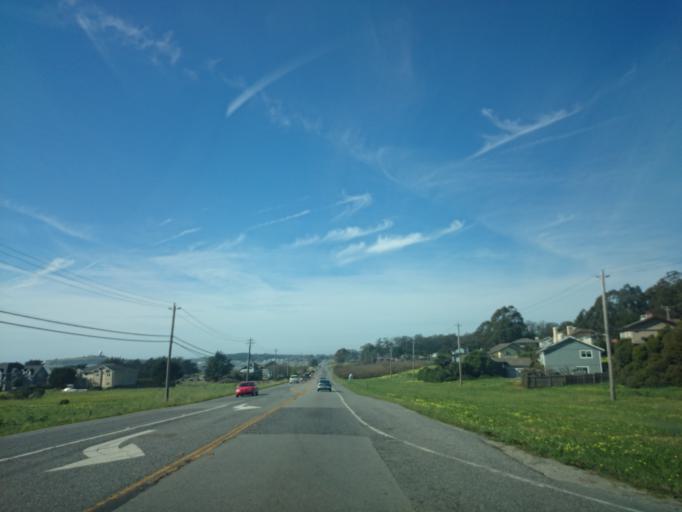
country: US
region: California
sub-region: San Mateo County
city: El Granada
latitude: 37.4961
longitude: -122.4577
